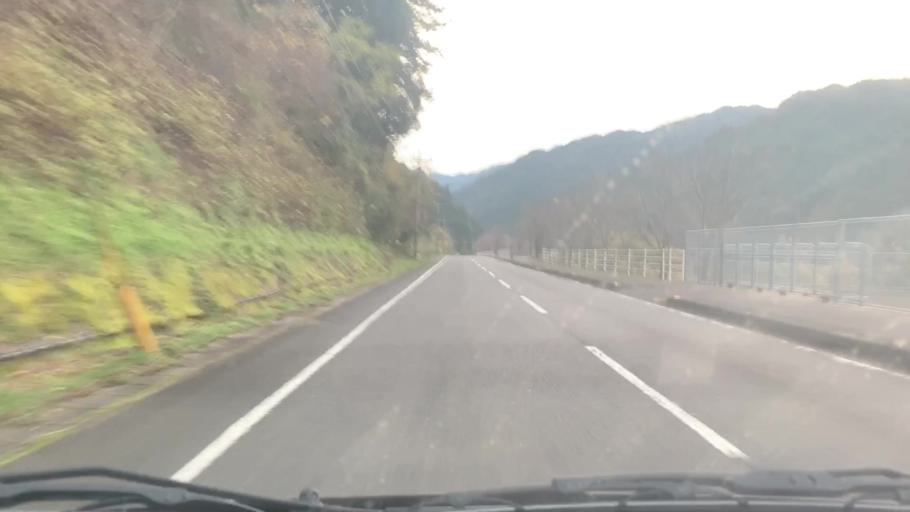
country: JP
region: Saga Prefecture
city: Kashima
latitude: 33.0345
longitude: 130.0700
